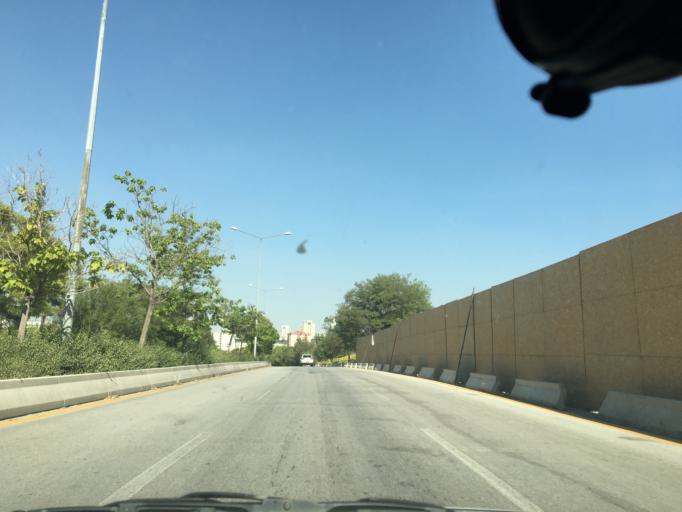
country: TR
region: Ankara
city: Ankara
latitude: 39.9175
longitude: 32.7919
